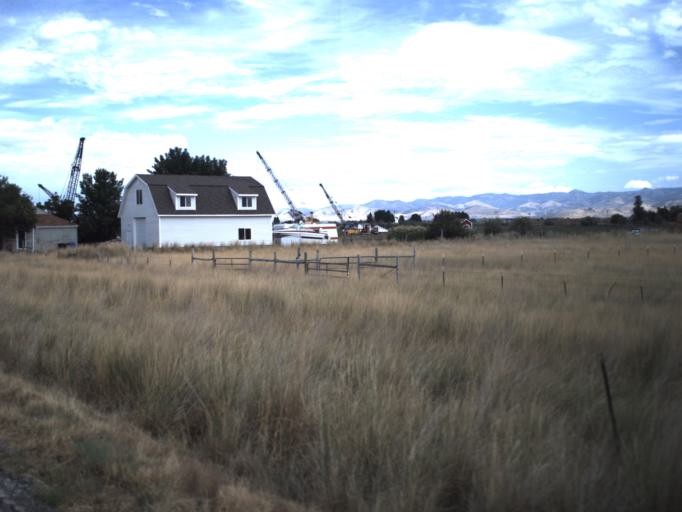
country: US
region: Utah
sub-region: Cache County
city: Lewiston
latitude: 41.9531
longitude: -111.9539
